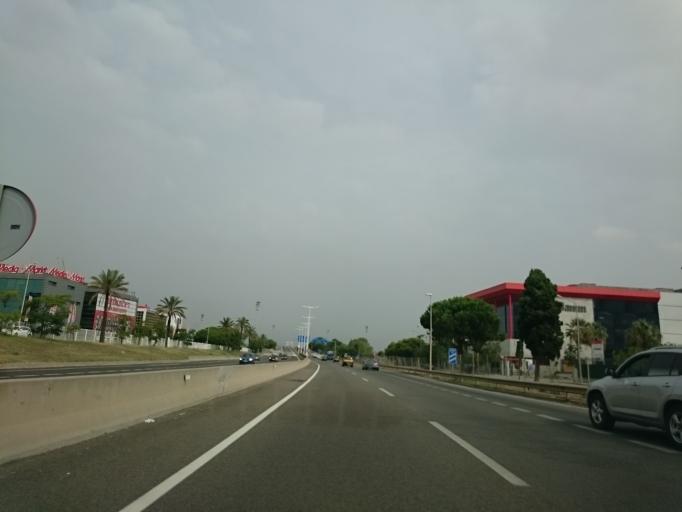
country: ES
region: Catalonia
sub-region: Provincia de Barcelona
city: El Prat de Llobregat
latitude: 41.3176
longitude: 2.0778
